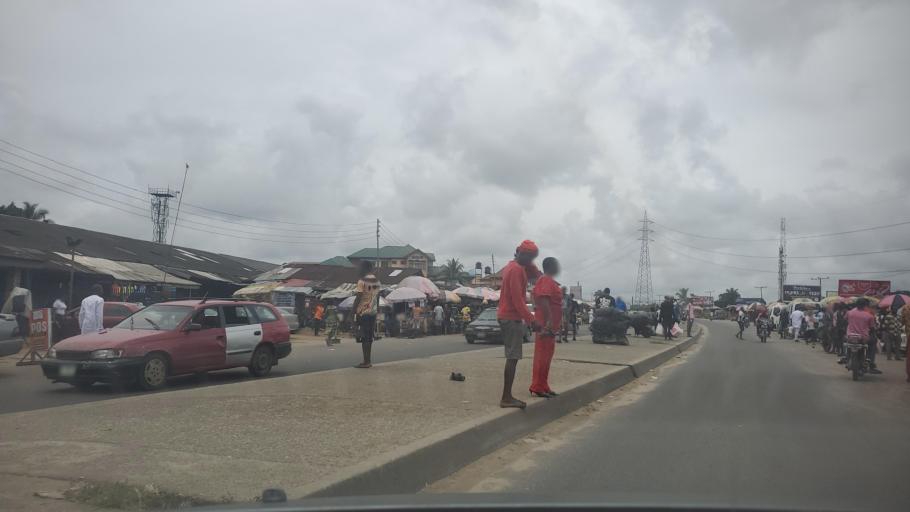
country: NG
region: Rivers
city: Emuoha
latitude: 4.8985
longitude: 6.9064
